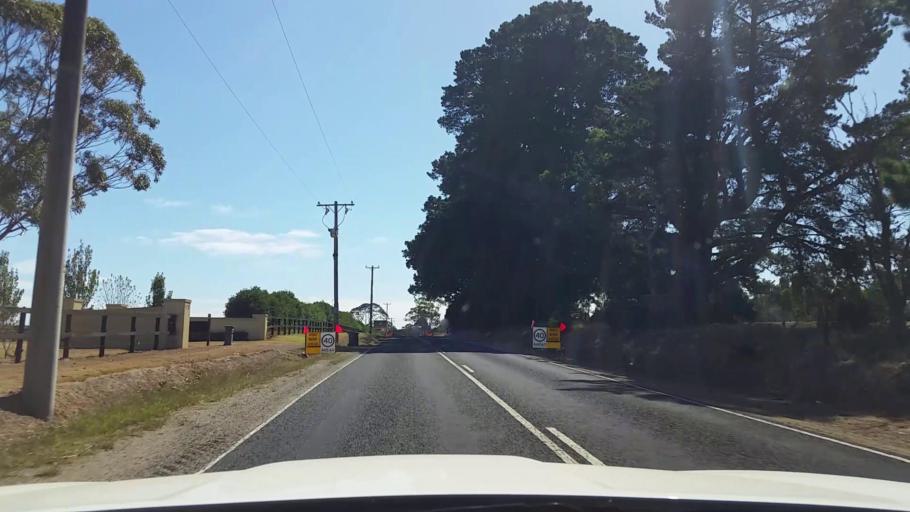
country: AU
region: Victoria
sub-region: Mornington Peninsula
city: Tyabb
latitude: -38.2623
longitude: 145.1456
